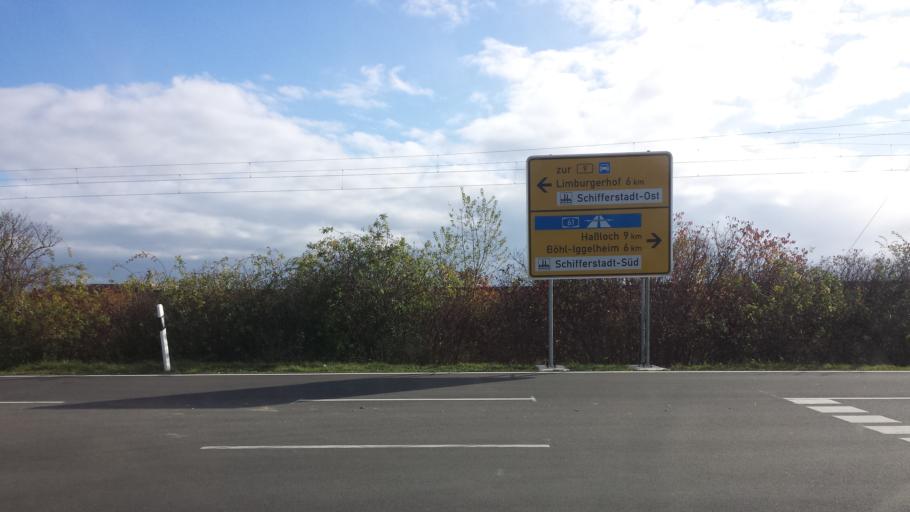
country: DE
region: Rheinland-Pfalz
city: Schifferstadt
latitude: 49.3945
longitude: 8.3559
